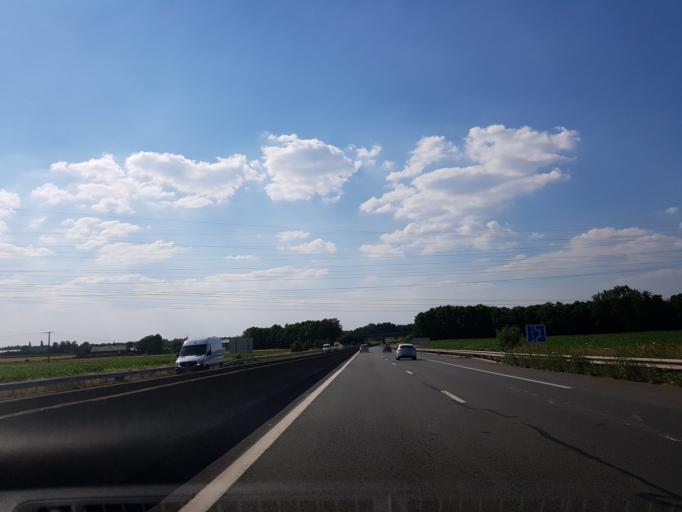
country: FR
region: Nord-Pas-de-Calais
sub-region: Departement du Nord
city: Escaudain
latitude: 50.3317
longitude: 3.3275
